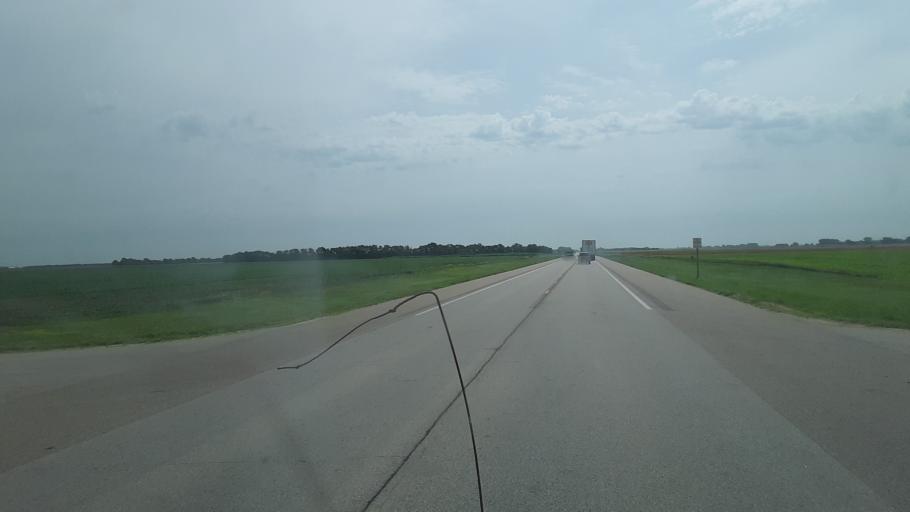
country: US
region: Kansas
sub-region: Reno County
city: Nickerson
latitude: 37.9855
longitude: -98.2164
